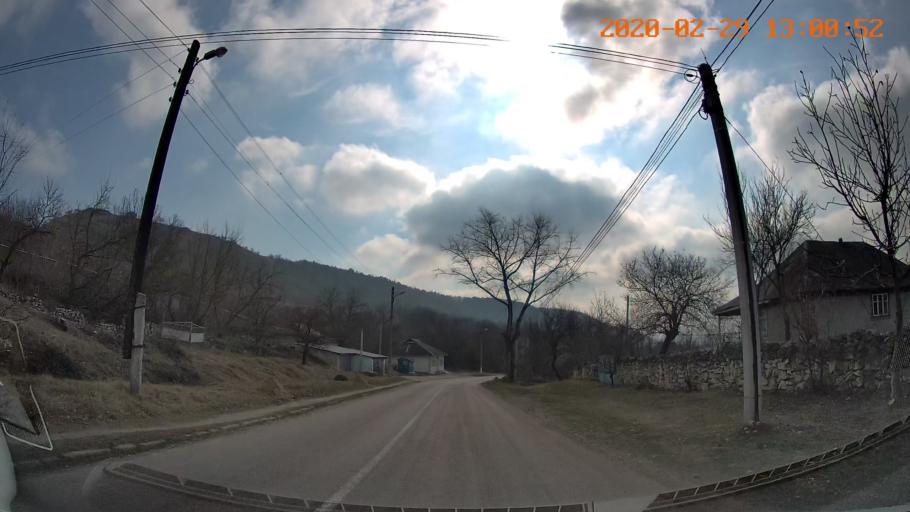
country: MD
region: Telenesti
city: Camenca
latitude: 48.0488
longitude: 28.7213
